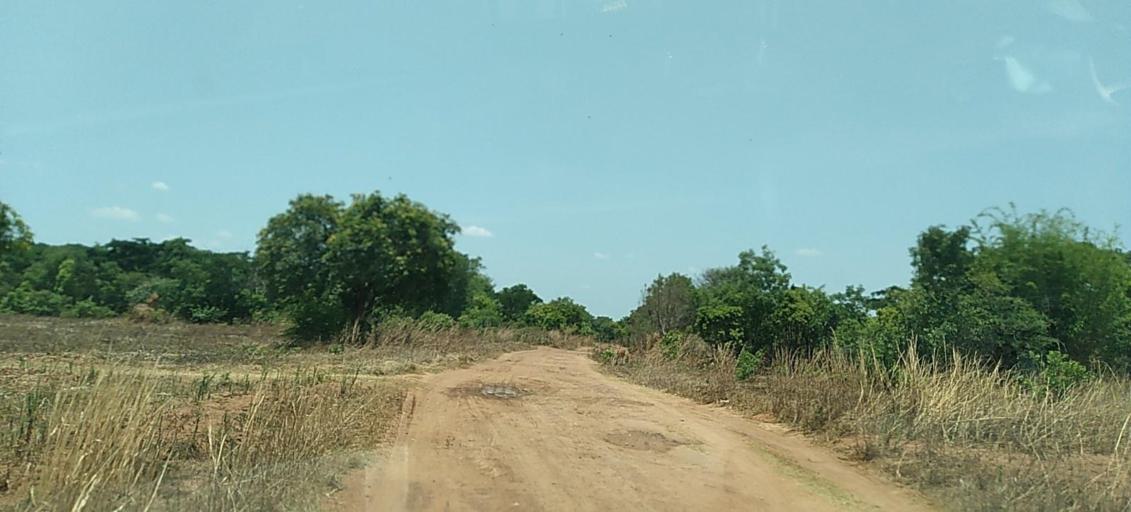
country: ZM
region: Copperbelt
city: Luanshya
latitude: -13.0988
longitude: 28.4053
